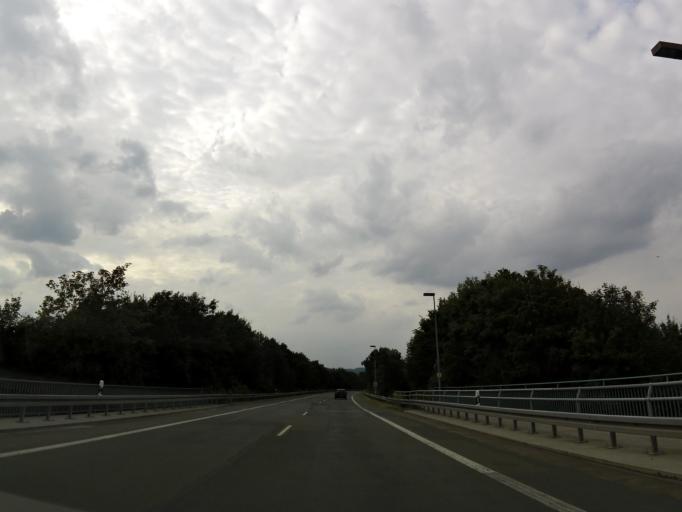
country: DE
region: North Rhine-Westphalia
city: Beverungen
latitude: 51.6382
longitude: 9.4039
